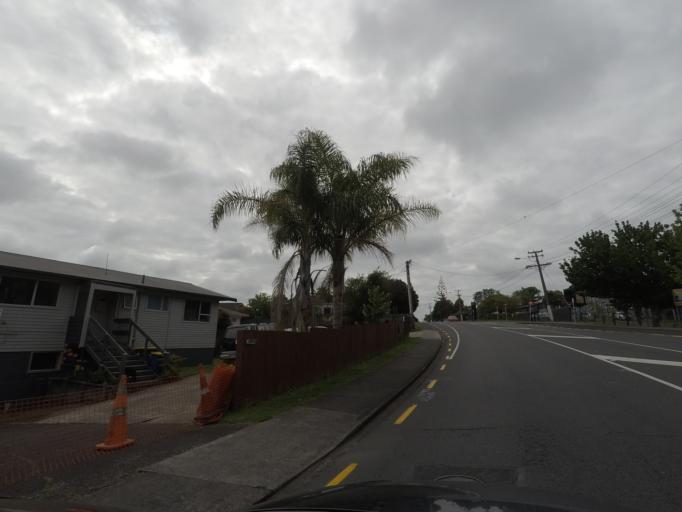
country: NZ
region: Auckland
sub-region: Auckland
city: Rosebank
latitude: -36.8412
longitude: 174.6007
